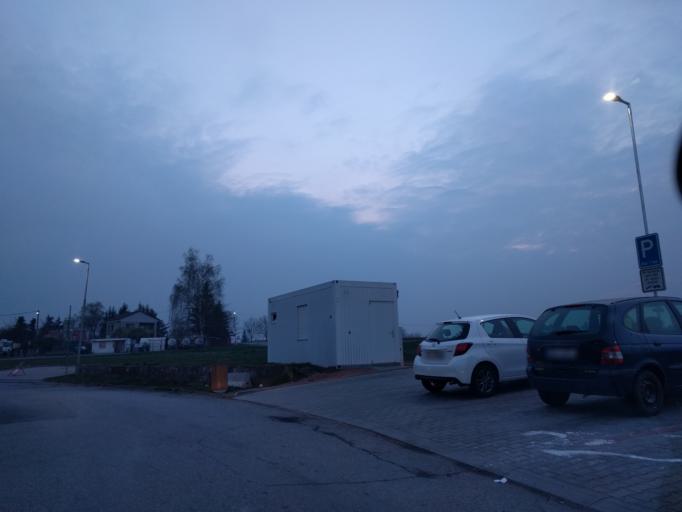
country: CZ
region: Central Bohemia
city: Luzna
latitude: 50.1729
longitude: 13.7412
